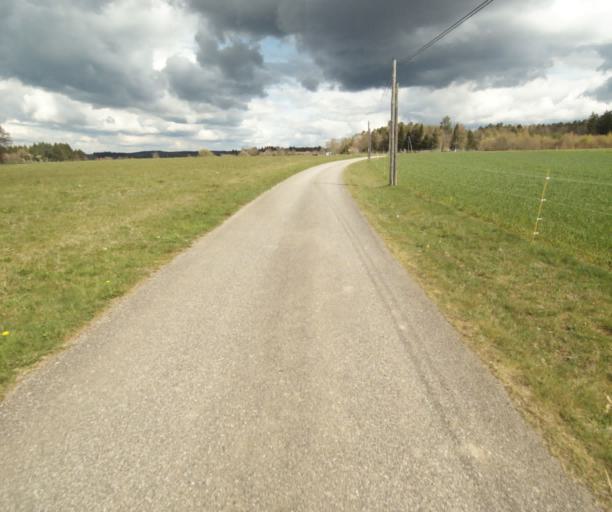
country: FR
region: Limousin
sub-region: Departement de la Correze
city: Laguenne
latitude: 45.2411
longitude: 1.8960
